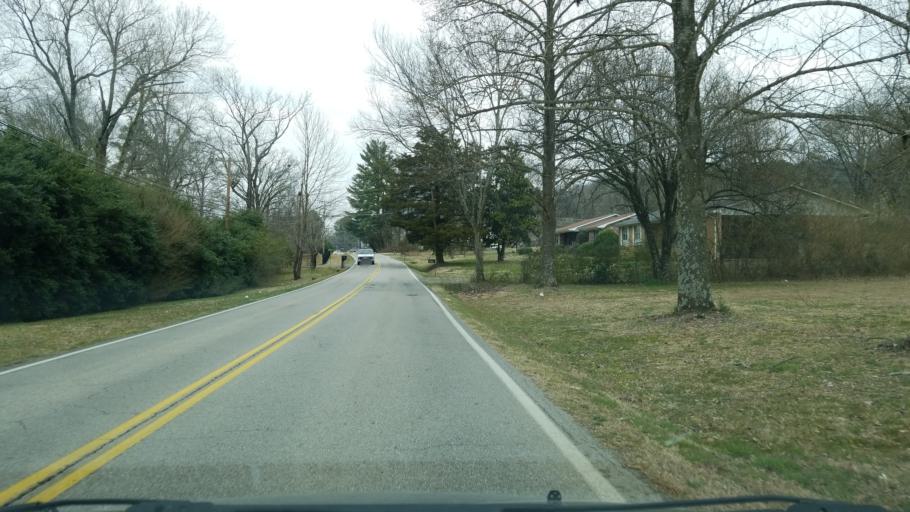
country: US
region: Tennessee
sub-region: Hamilton County
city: East Brainerd
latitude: 35.0104
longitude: -85.1277
